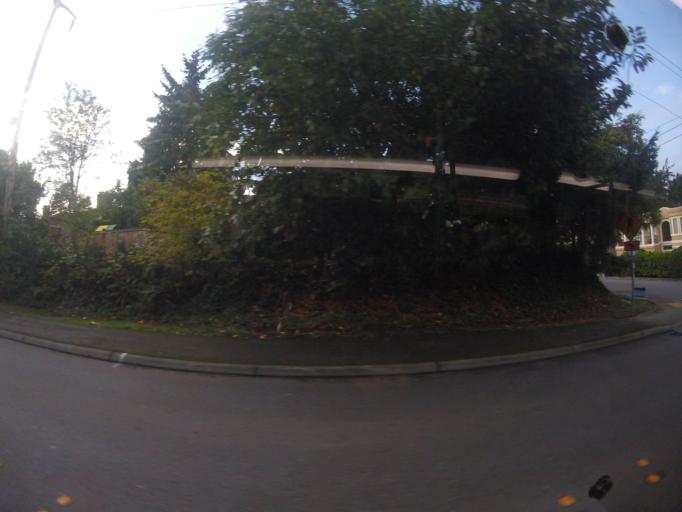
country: US
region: Washington
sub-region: King County
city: Bellevue
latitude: 47.6175
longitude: -122.2131
